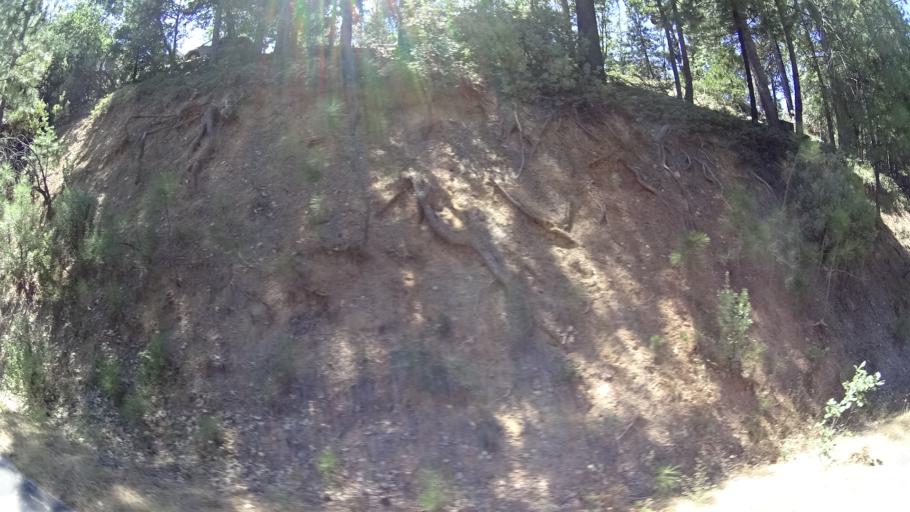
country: US
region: California
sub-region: Calaveras County
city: Forest Meadows
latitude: 38.1898
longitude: -120.3565
